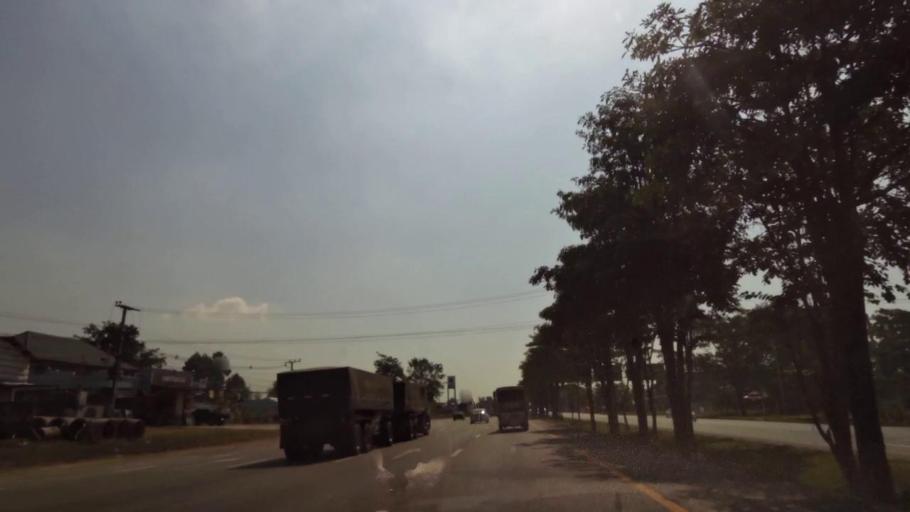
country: TH
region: Phichit
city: Bueng Na Rang
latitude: 16.1215
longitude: 100.1257
